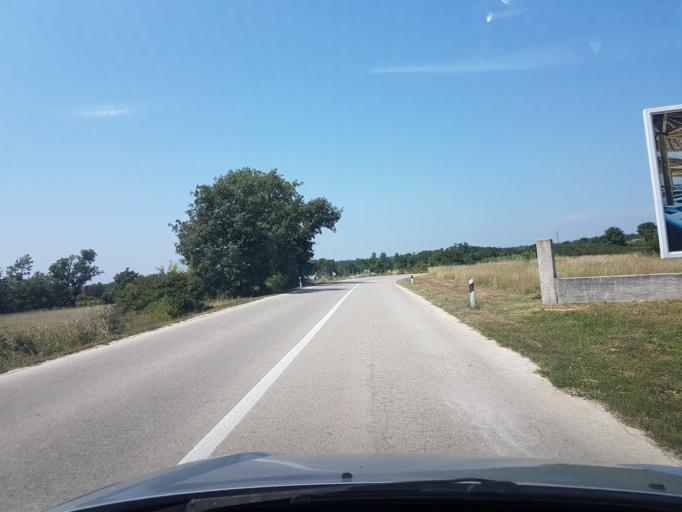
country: HR
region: Istarska
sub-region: Grad Rovinj
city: Rovinj
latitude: 45.1476
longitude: 13.6992
